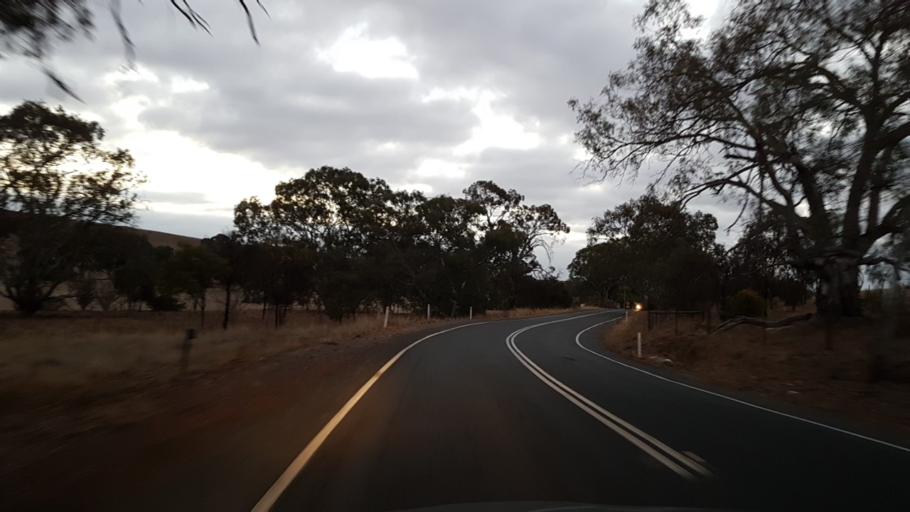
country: AU
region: South Australia
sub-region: Mount Barker
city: Nairne
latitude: -35.0327
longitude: 138.9718
